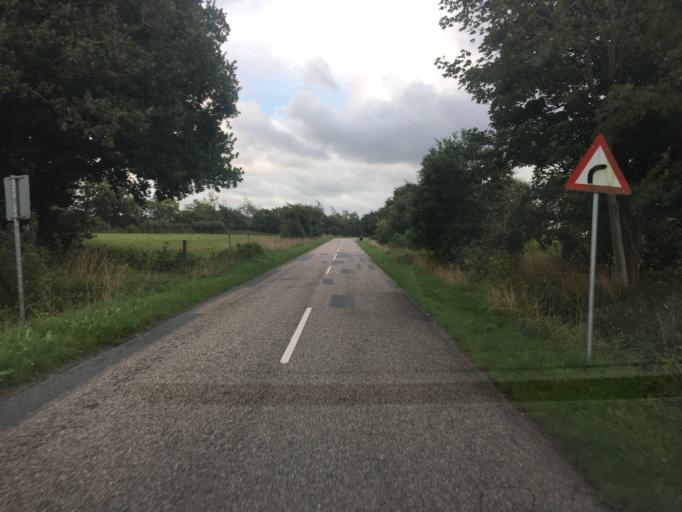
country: DK
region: South Denmark
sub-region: Tonder Kommune
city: Tonder
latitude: 54.9551
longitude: 8.8203
